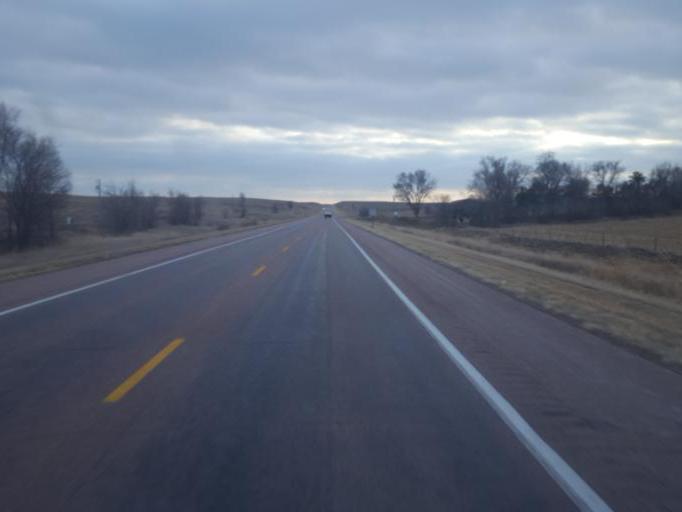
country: US
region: Nebraska
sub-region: Cedar County
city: Hartington
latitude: 42.6693
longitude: -97.4263
